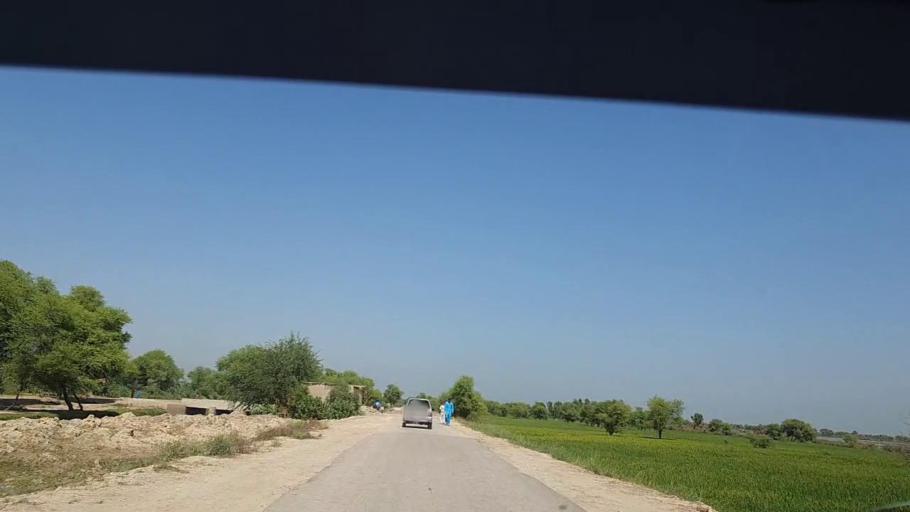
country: PK
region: Sindh
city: Kandhkot
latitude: 28.3034
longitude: 69.1116
